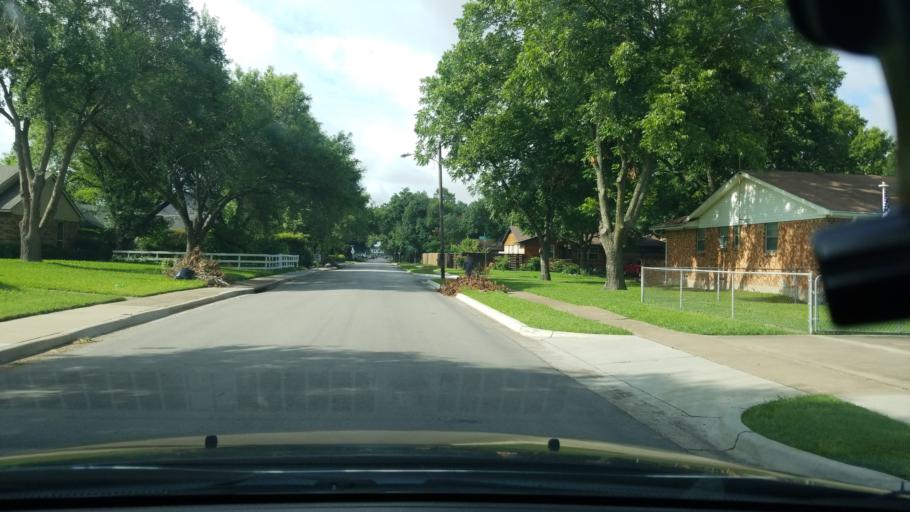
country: US
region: Texas
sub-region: Dallas County
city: Mesquite
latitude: 32.8156
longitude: -96.6685
